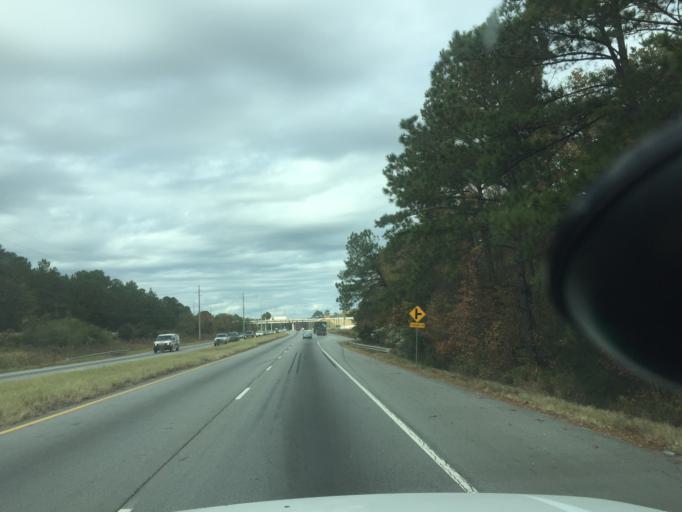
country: US
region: Georgia
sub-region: Chatham County
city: Port Wentworth
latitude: 32.1587
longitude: -81.1825
